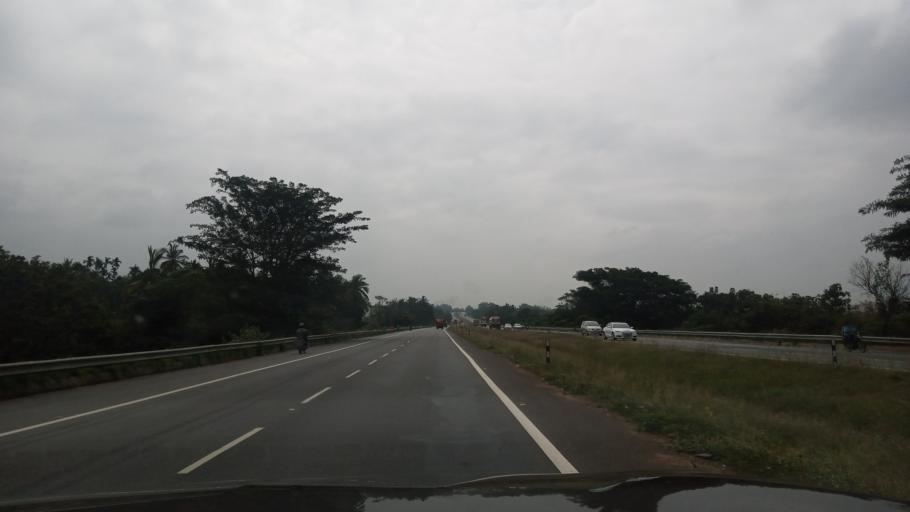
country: IN
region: Karnataka
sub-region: Bangalore Urban
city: Bangalore
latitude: 12.9376
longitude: 77.4696
